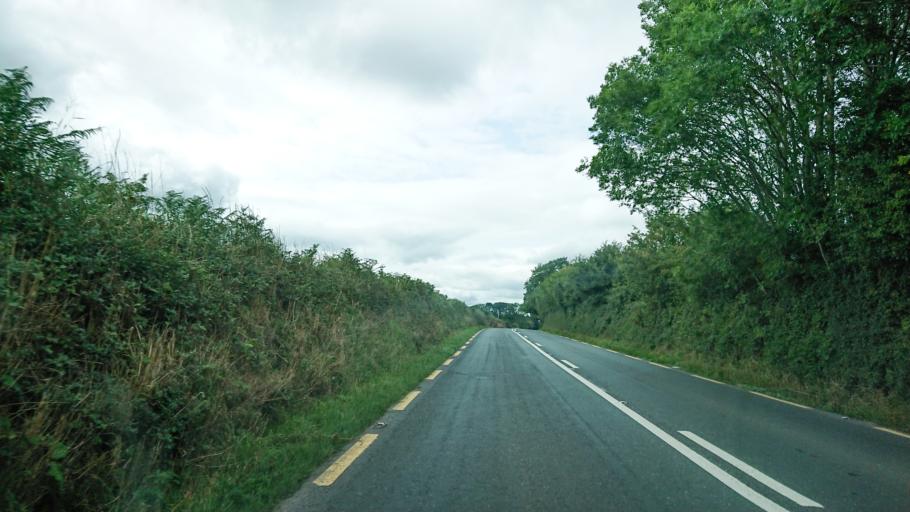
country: IE
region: Munster
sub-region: Waterford
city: Dungarvan
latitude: 52.1108
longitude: -7.6910
